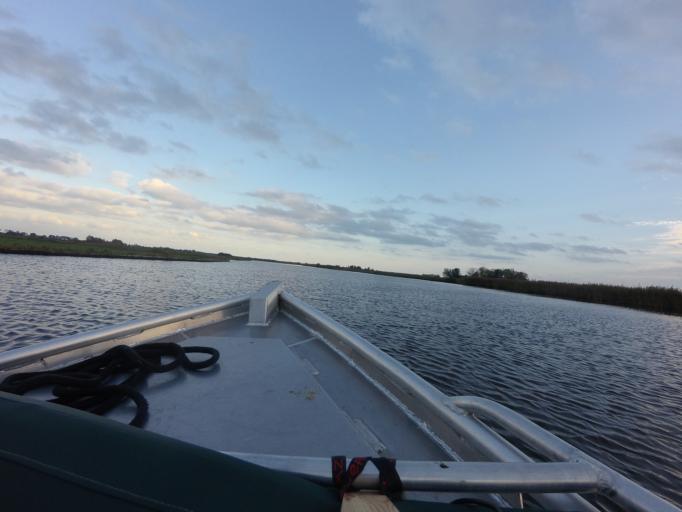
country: NL
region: Overijssel
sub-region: Gemeente Steenwijkerland
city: Blokzijl
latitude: 52.7315
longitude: 5.9843
